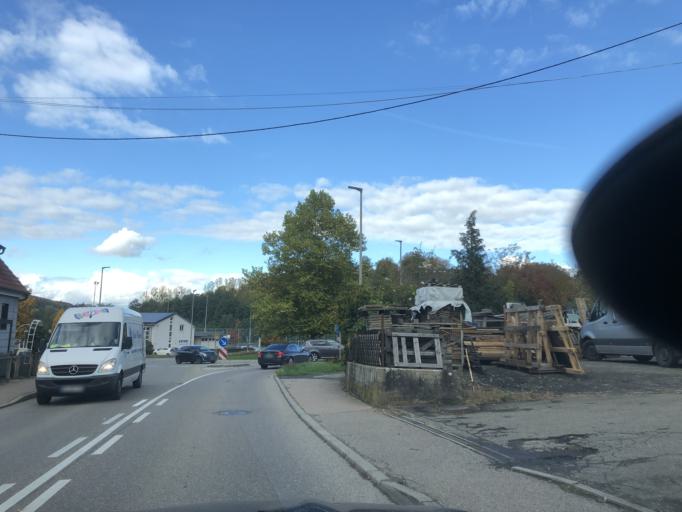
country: DE
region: Baden-Wuerttemberg
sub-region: Regierungsbezirk Stuttgart
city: Winterbach
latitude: 48.8476
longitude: 9.4533
